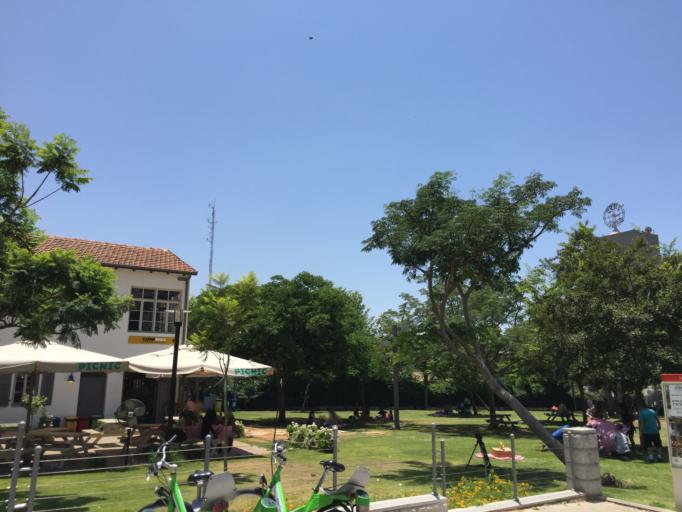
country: IL
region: Tel Aviv
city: Tel Aviv
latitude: 32.0733
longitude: 34.7858
